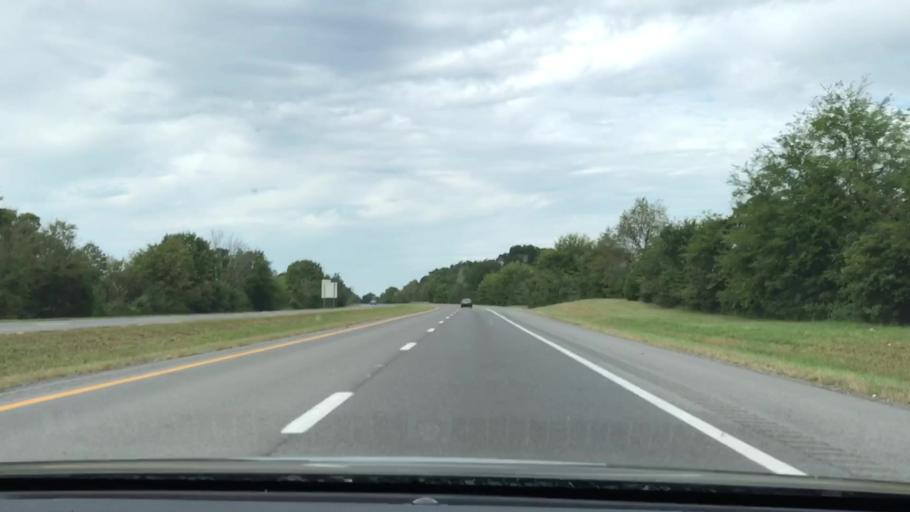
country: US
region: Kentucky
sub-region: Marshall County
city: Benton
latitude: 36.8472
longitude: -88.3992
